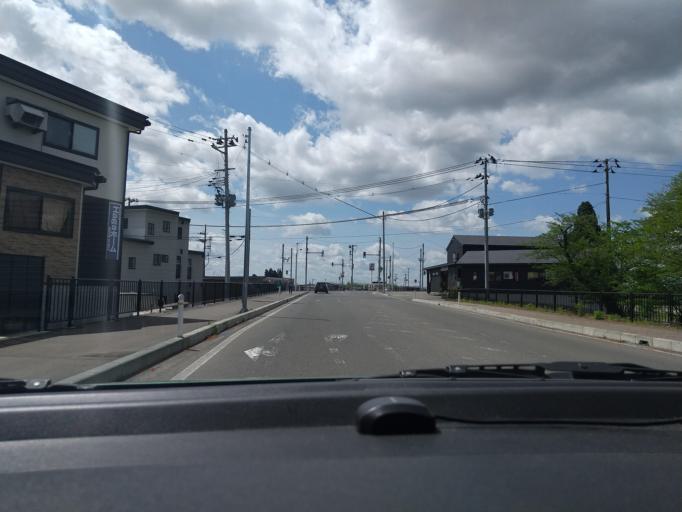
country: JP
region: Akita
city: Kakunodatemachi
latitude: 39.5921
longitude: 140.5601
